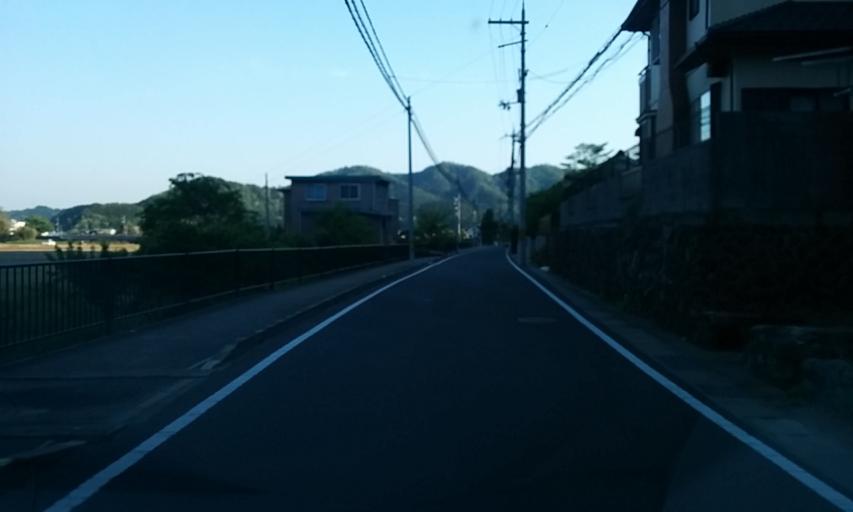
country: JP
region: Kyoto
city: Kameoka
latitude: 35.0832
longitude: 135.5166
